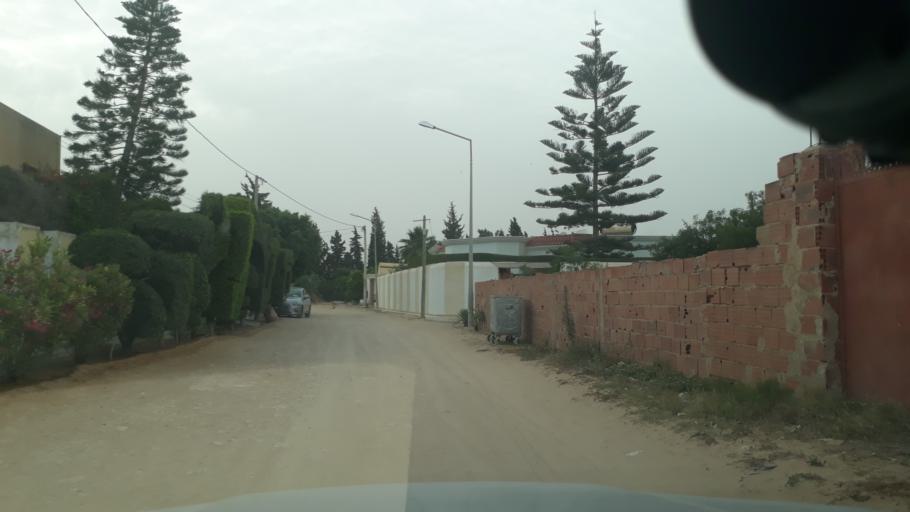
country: TN
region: Safaqis
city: Al Qarmadah
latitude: 34.7836
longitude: 10.7715
